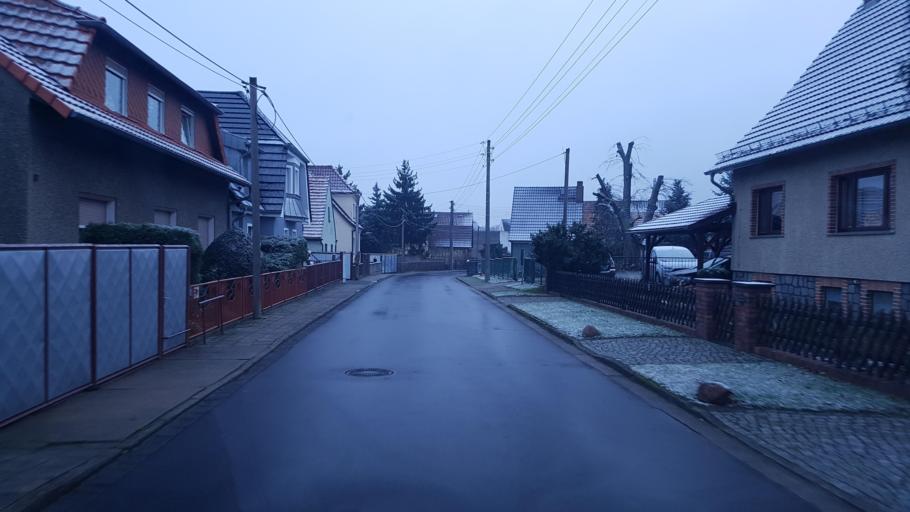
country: DE
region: Brandenburg
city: Kasel-Golzig
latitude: 51.9366
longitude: 13.7797
